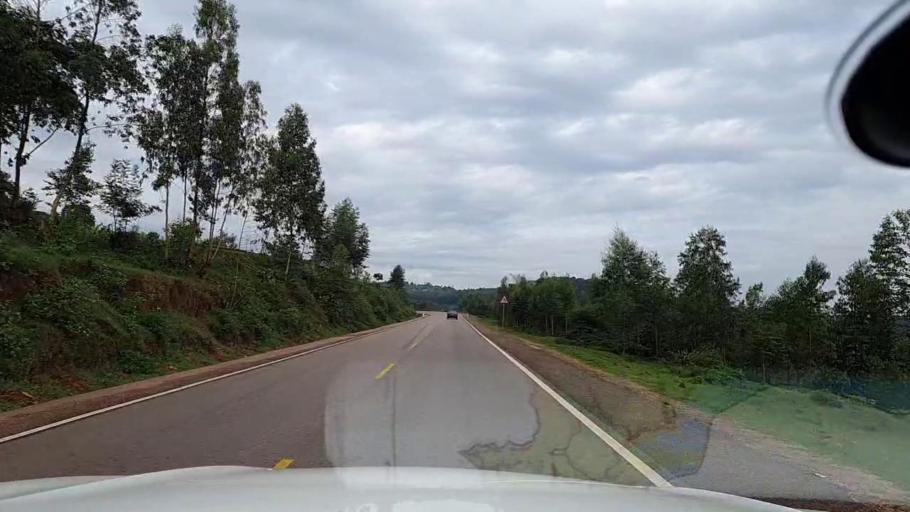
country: RW
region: Southern Province
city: Butare
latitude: -2.5600
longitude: 29.7188
